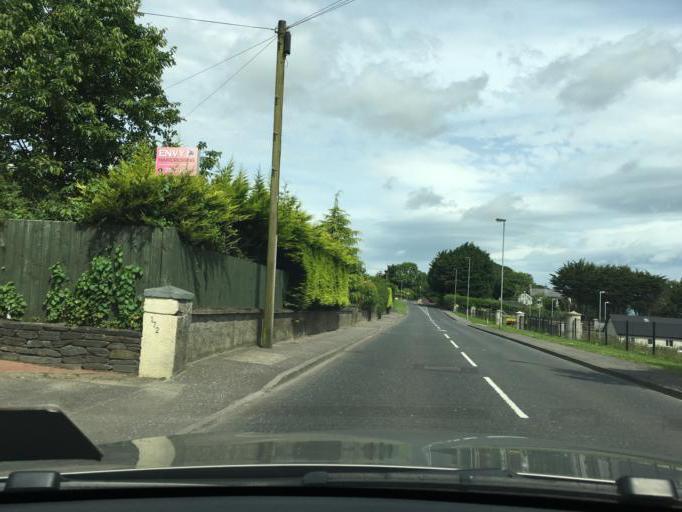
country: GB
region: Northern Ireland
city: Culmore
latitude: 55.0465
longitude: -7.2743
